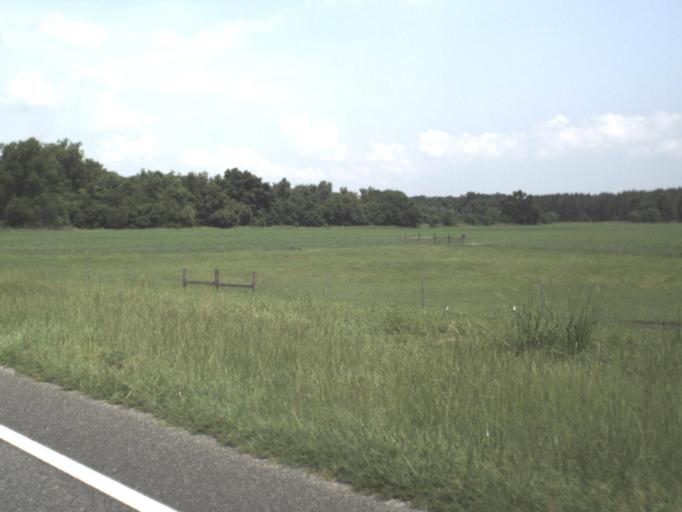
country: US
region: Florida
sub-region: Levy County
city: Chiefland
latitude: 29.4751
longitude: -82.7898
